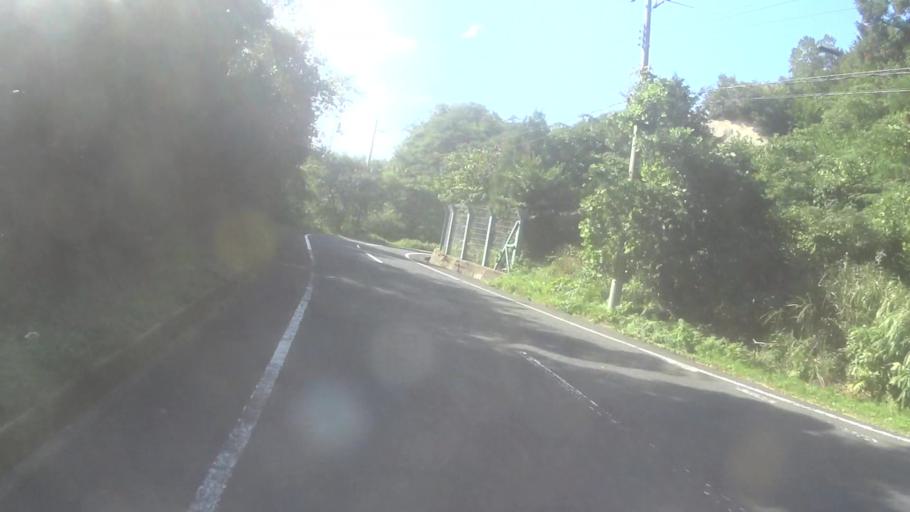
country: JP
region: Kyoto
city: Miyazu
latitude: 35.6940
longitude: 135.1462
